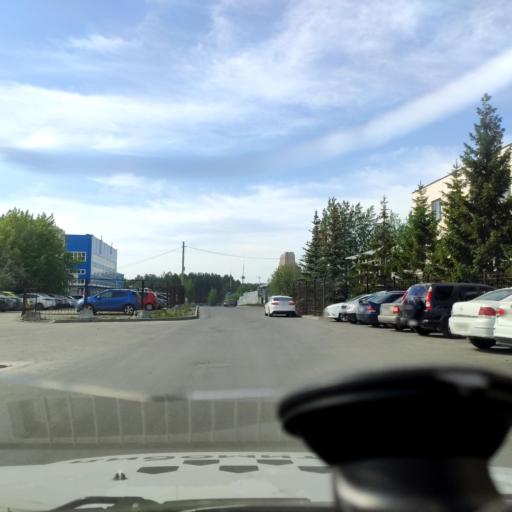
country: RU
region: Sverdlovsk
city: Sovkhoznyy
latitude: 56.7722
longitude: 60.5572
